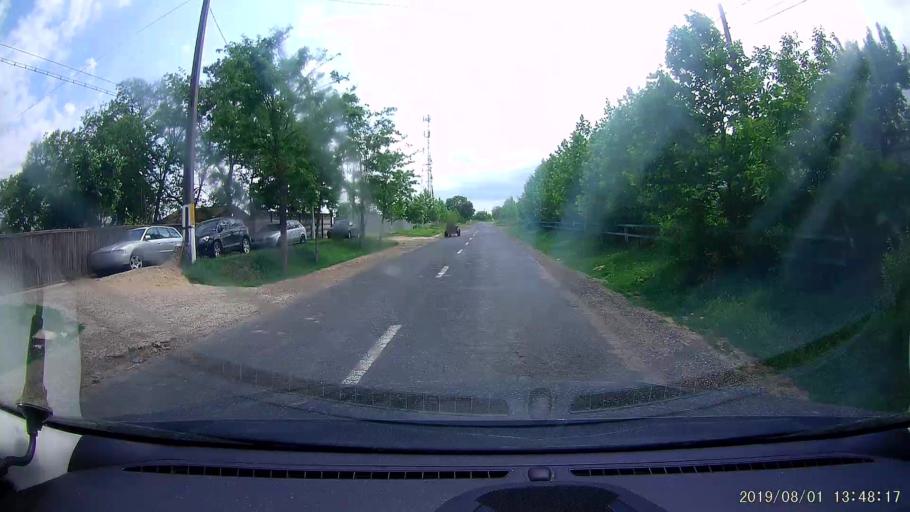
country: RO
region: Galati
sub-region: Comuna Oancea
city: Oancea
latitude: 45.9097
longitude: 28.1121
